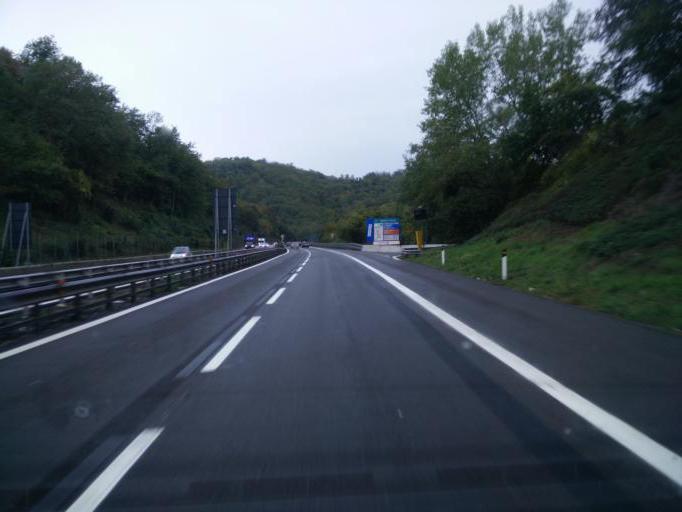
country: IT
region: Tuscany
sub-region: Province of Florence
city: Barberino di Mugello
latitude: 44.0540
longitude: 11.2161
